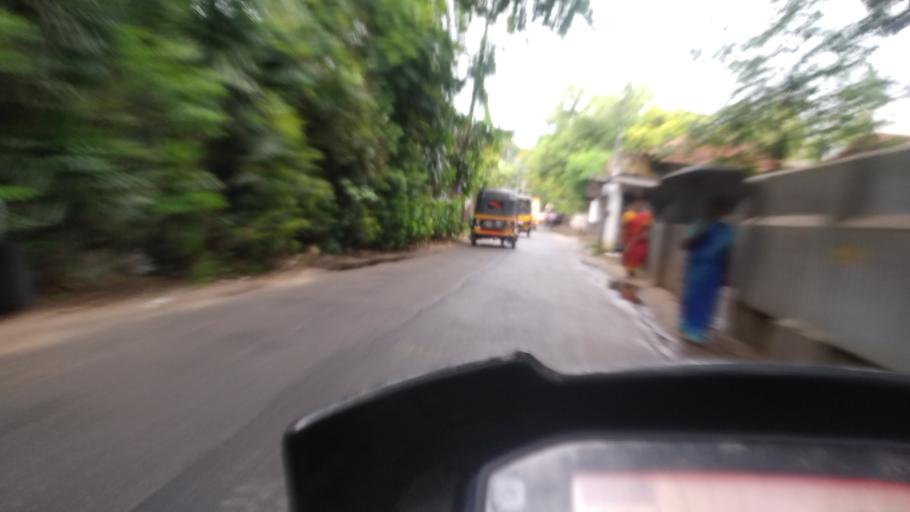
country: IN
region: Kerala
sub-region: Alappuzha
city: Alleppey
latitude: 9.5014
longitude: 76.3214
